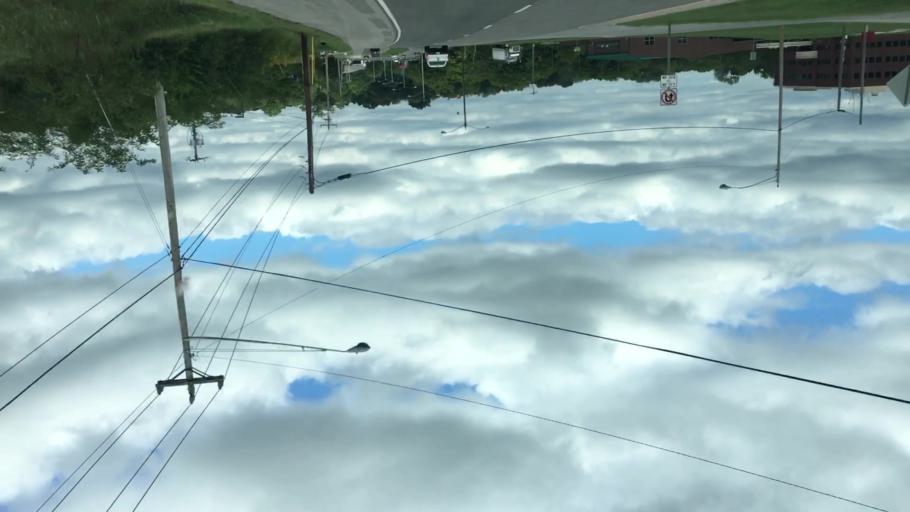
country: US
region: Tennessee
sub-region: Maury County
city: Columbia
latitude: 35.6121
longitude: -87.0682
